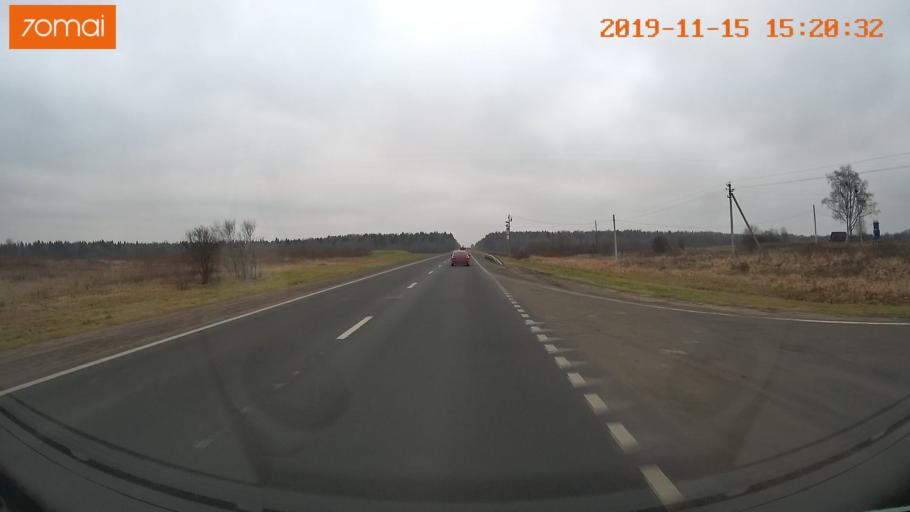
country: RU
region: Jaroslavl
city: Danilov
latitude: 58.2225
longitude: 40.1602
